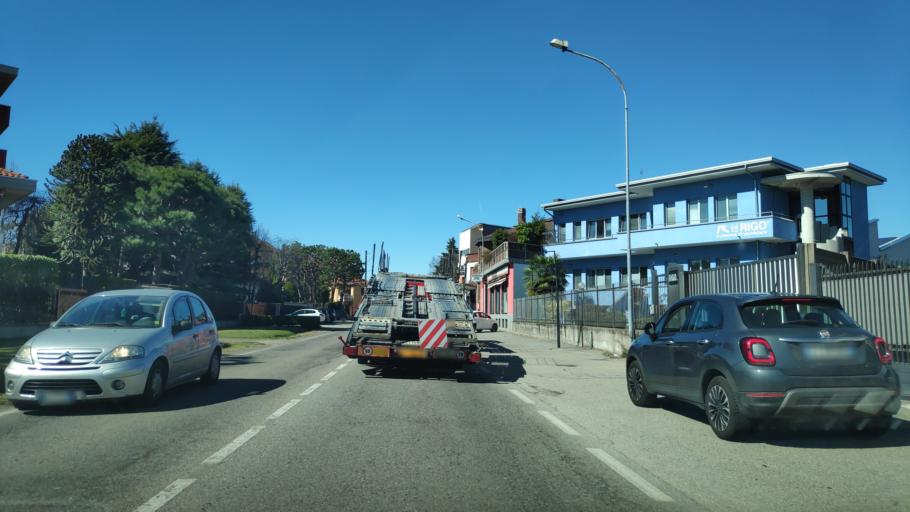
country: IT
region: Lombardy
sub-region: Provincia di Varese
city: Olgiate Olona
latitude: 45.6176
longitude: 8.8755
